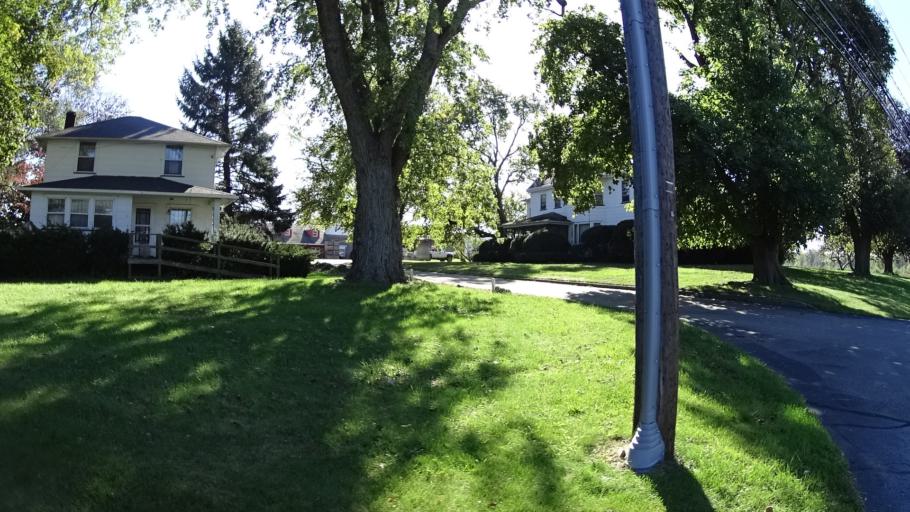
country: US
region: Ohio
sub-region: Lorain County
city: Lorain
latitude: 41.4155
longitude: -82.1625
